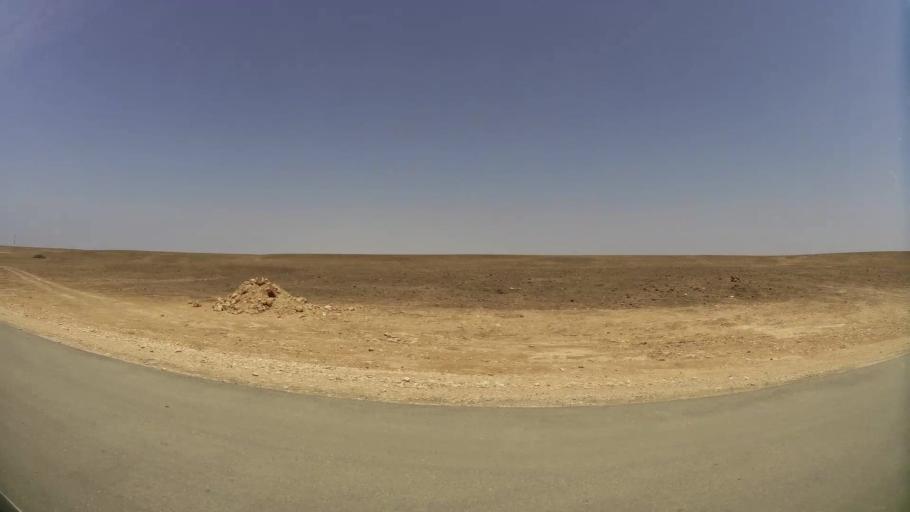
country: OM
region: Zufar
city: Salalah
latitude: 17.0792
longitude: 54.1802
